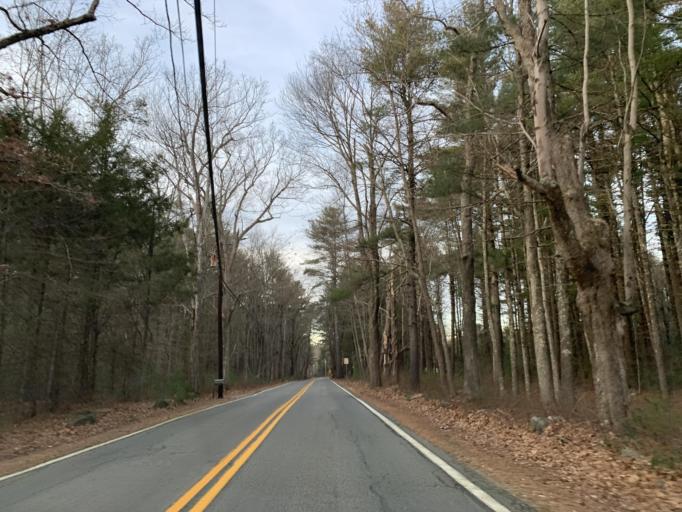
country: US
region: Rhode Island
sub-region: Providence County
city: Pascoag
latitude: 41.9287
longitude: -71.6997
